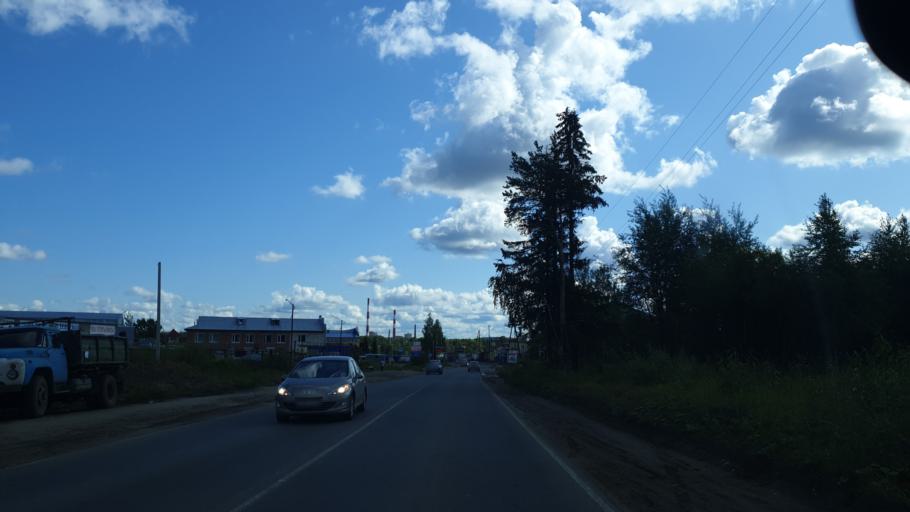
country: RU
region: Komi Republic
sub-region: Syktyvdinskiy Rayon
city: Syktyvkar
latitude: 61.6760
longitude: 50.7693
